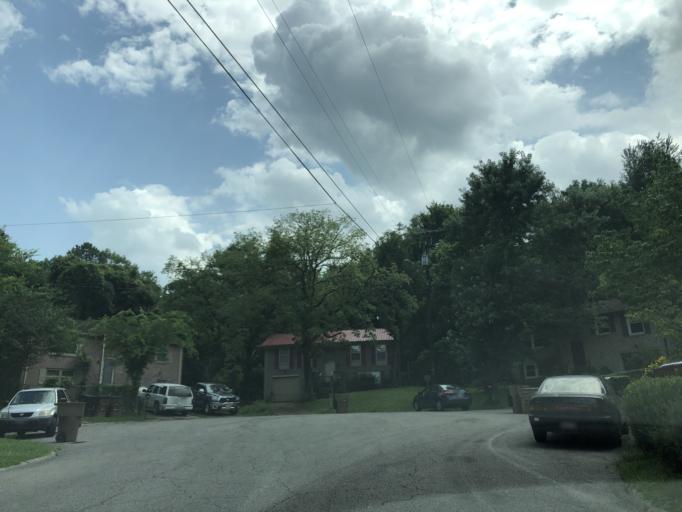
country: US
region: Tennessee
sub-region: Williamson County
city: Brentwood Estates
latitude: 36.0594
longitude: -86.6875
